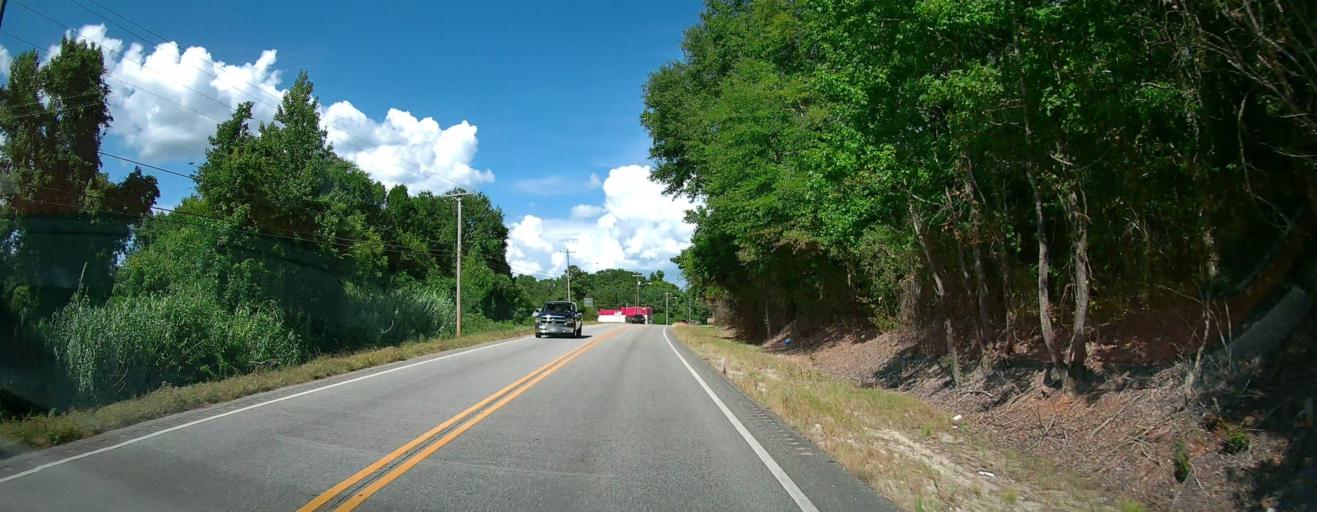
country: US
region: Alabama
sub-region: Macon County
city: Tuskegee
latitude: 32.4383
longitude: -85.6684
